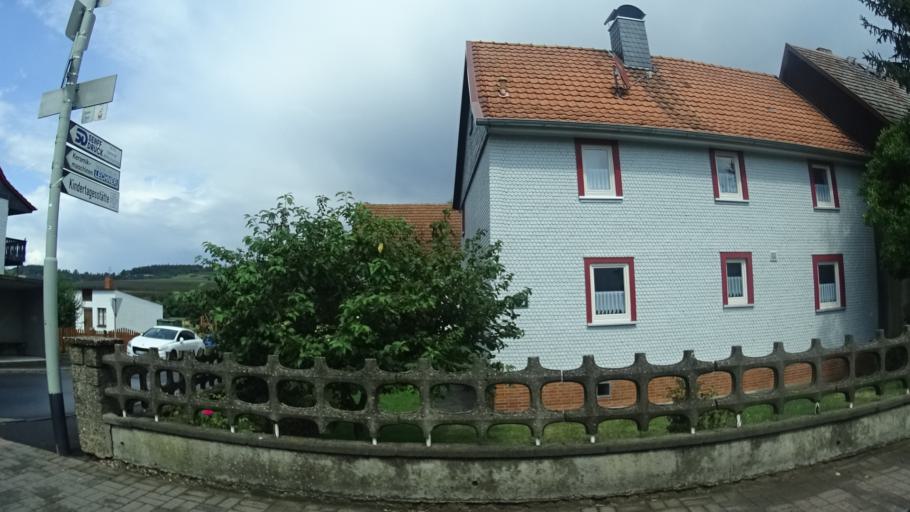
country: DE
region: Hesse
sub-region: Regierungsbezirk Giessen
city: Lauterbach
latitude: 50.6299
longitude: 9.4422
